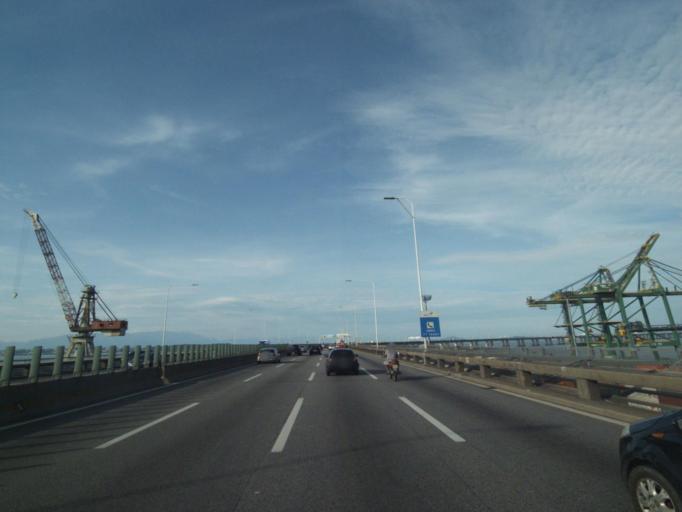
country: BR
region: Rio de Janeiro
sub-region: Rio De Janeiro
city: Rio de Janeiro
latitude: -22.8726
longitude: -43.2052
